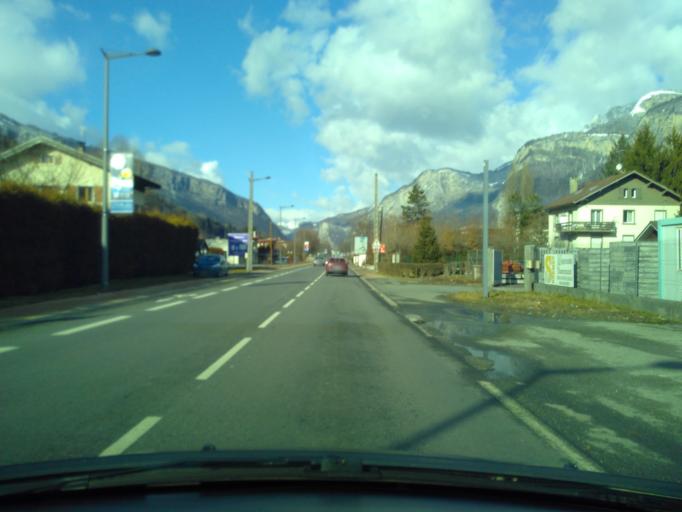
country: FR
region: Rhone-Alpes
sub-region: Departement de la Haute-Savoie
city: Sallanches
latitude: 45.9476
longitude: 6.6300
